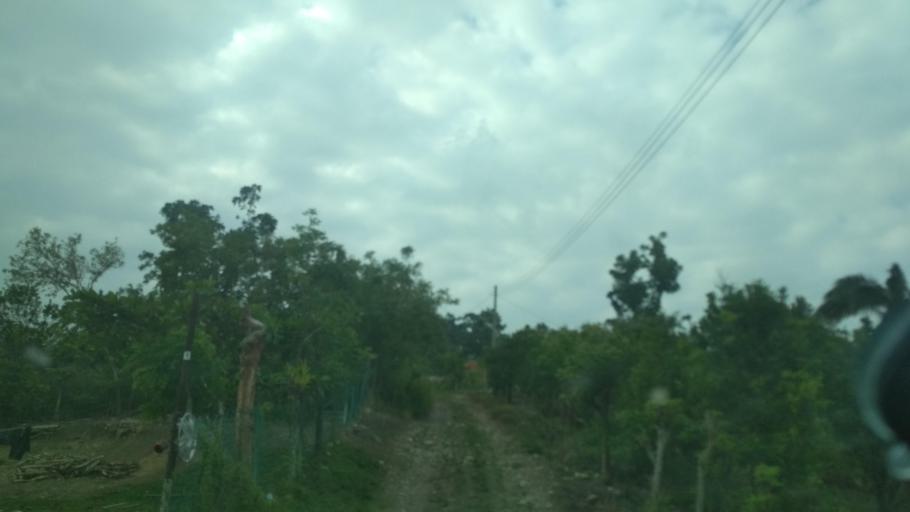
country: MX
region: Veracruz
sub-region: Poza Rica de Hidalgo
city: El Mollejon
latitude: 20.5225
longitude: -97.3797
